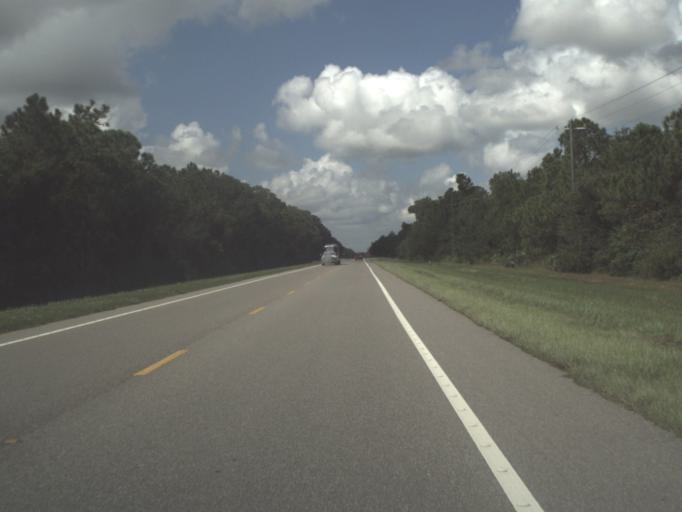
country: US
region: Florida
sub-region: Sarasota County
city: The Meadows
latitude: 27.4086
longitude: -82.3312
